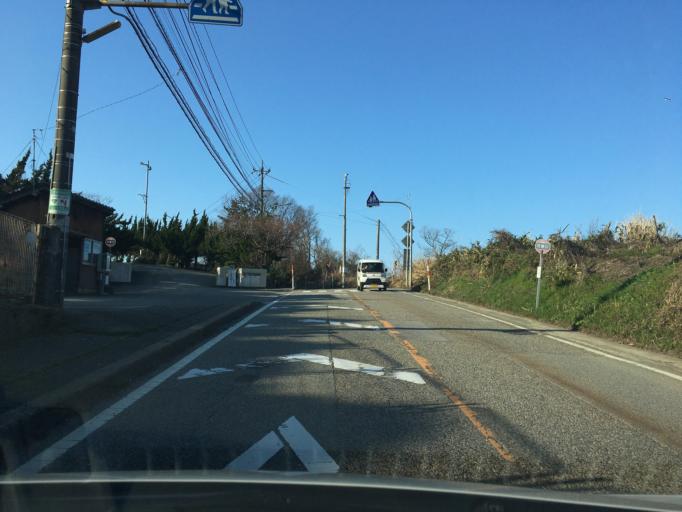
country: JP
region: Ishikawa
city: Nanao
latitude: 36.9820
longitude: 137.0497
